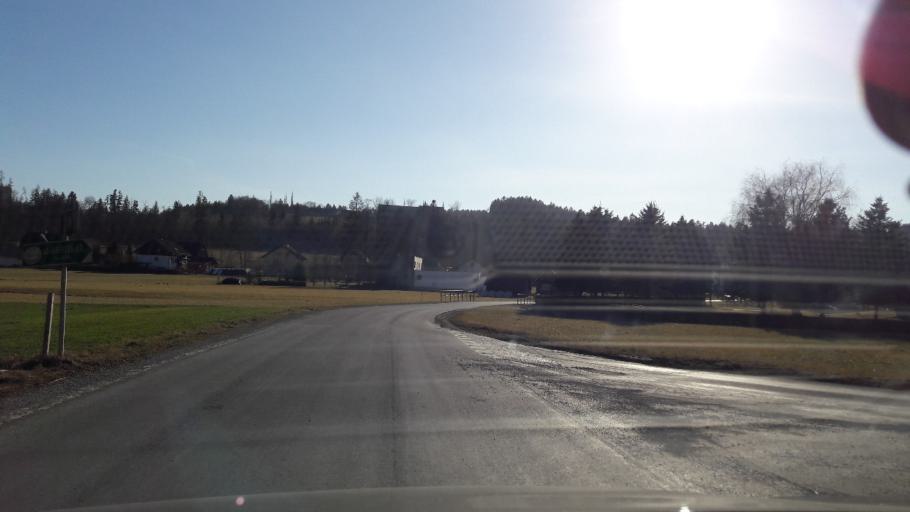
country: AT
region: Styria
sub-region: Politischer Bezirk Graz-Umgebung
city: Eisbach
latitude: 47.1074
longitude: 15.2737
